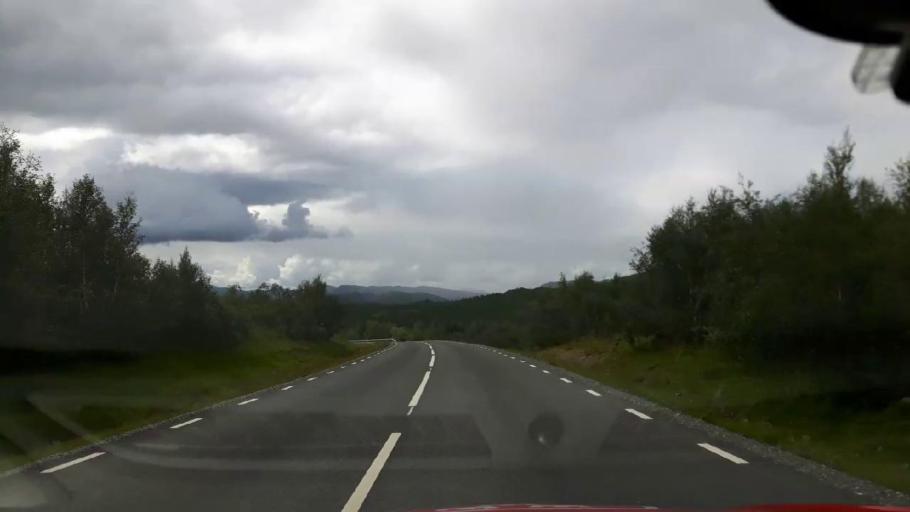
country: NO
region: Nordland
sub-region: Hattfjelldal
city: Hattfjelldal
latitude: 64.9874
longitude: 14.2151
